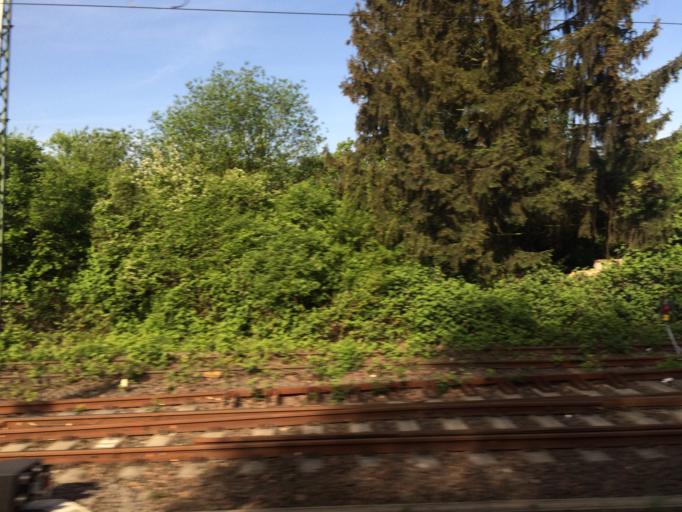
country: DE
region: North Rhine-Westphalia
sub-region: Regierungsbezirk Koln
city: Konigswinter
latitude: 50.7031
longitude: 7.1730
